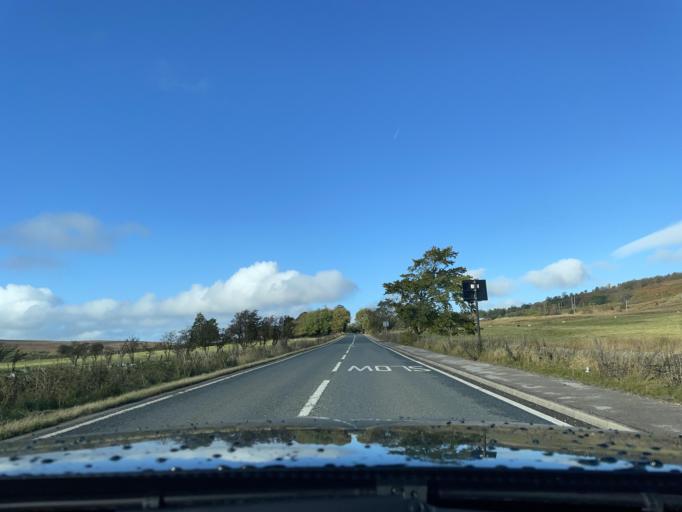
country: GB
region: England
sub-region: Sheffield
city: Bradfield
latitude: 53.3863
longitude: -1.6250
